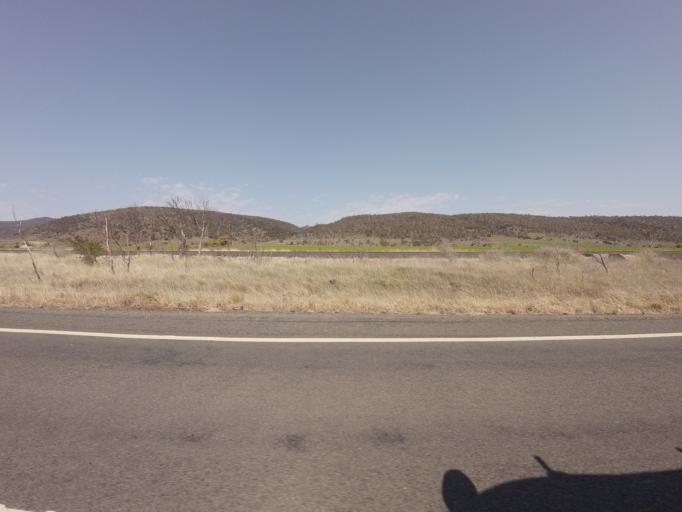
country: AU
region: Tasmania
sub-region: Northern Midlands
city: Evandale
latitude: -41.8117
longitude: 147.6295
